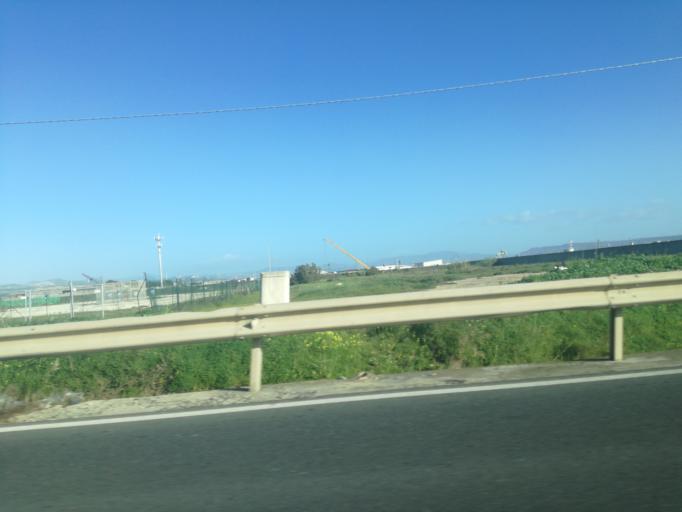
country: IT
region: Sicily
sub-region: Provincia di Caltanissetta
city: Gela
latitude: 37.0586
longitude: 14.2858
